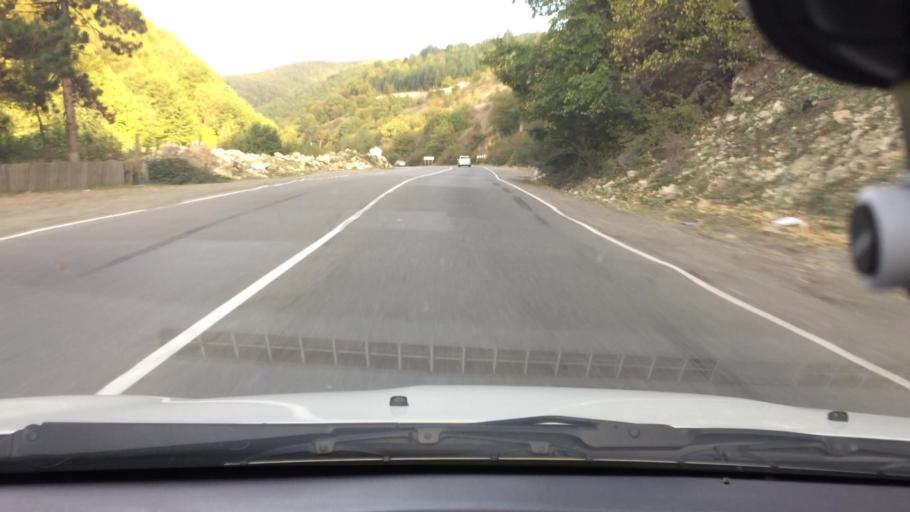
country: GE
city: Surami
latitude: 42.0366
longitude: 43.5191
